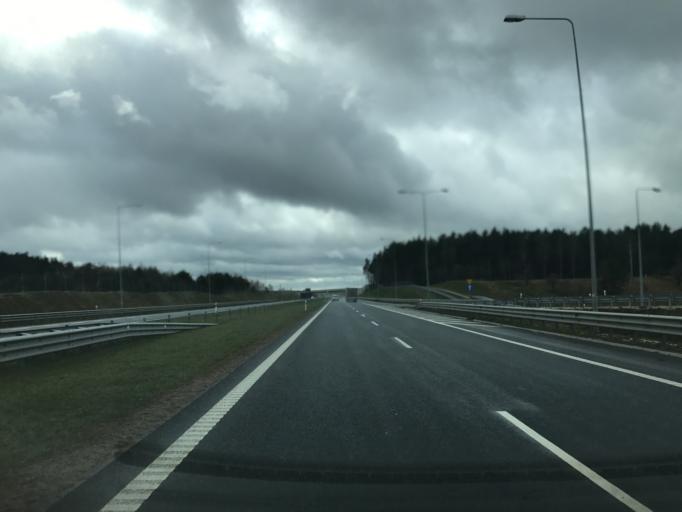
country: PL
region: Warmian-Masurian Voivodeship
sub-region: Powiat olsztynski
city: Olsztynek
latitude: 53.6038
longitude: 20.3037
